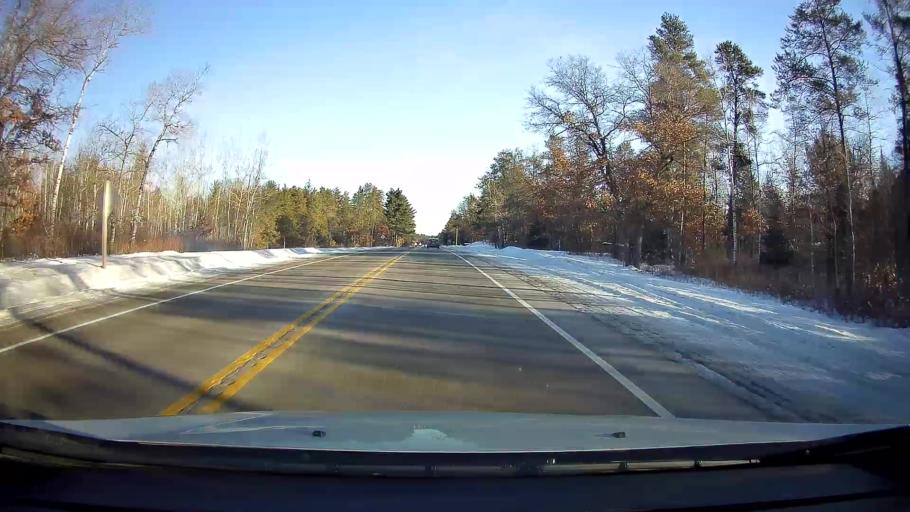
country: US
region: Wisconsin
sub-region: Sawyer County
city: Hayward
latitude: 45.9519
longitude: -91.6844
